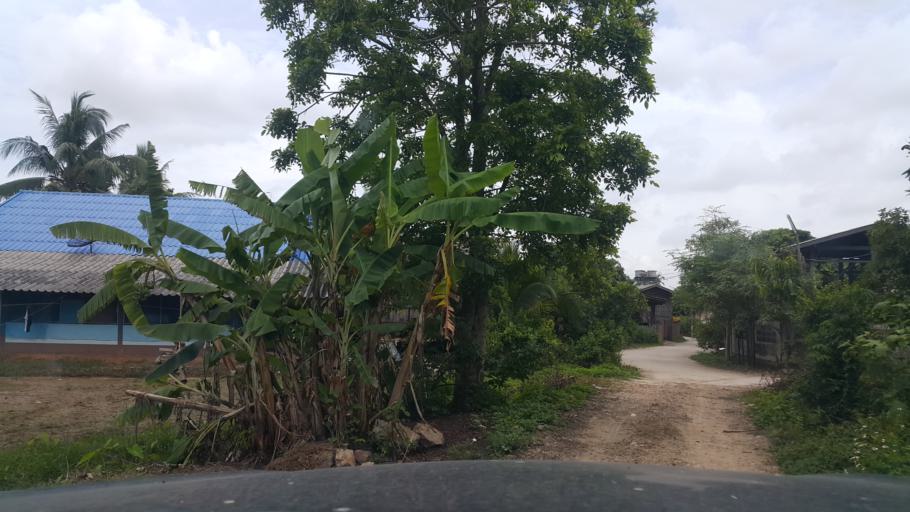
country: TH
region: Lamphun
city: Ban Thi
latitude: 18.6429
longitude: 99.1444
